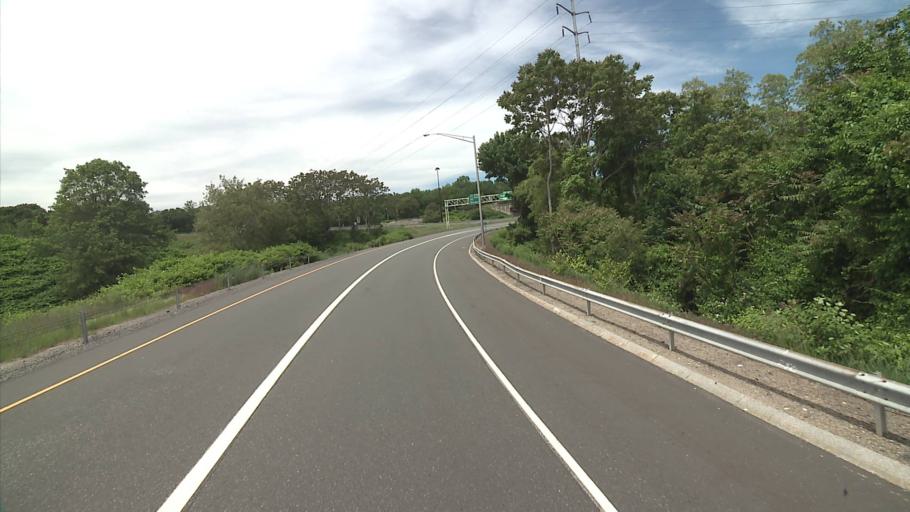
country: US
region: Connecticut
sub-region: New London County
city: New London
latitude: 41.3680
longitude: -72.1048
